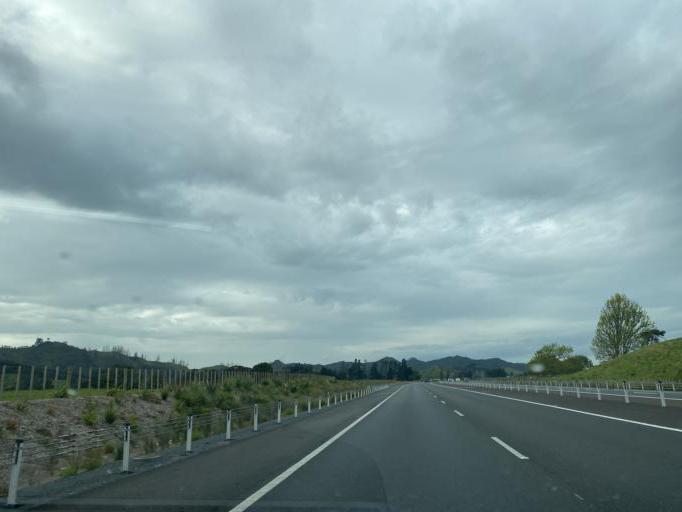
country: NZ
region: Waikato
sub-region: Waikato District
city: Ngaruawahia
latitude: -37.6116
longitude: 175.2047
